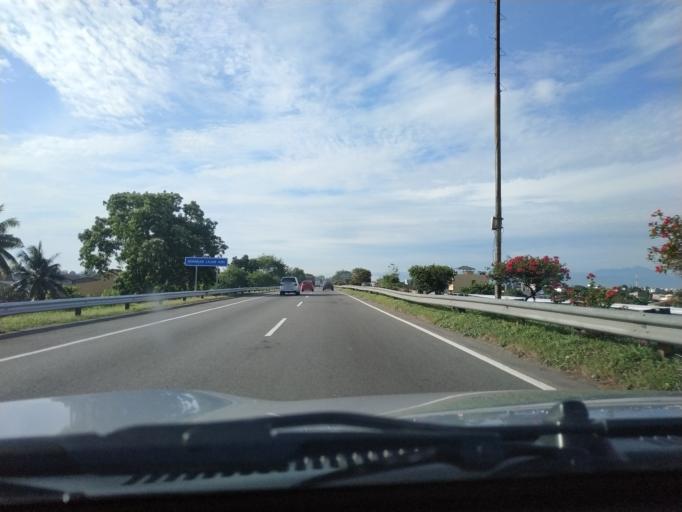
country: ID
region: North Sumatra
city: Medan
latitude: 3.5901
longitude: 98.7241
